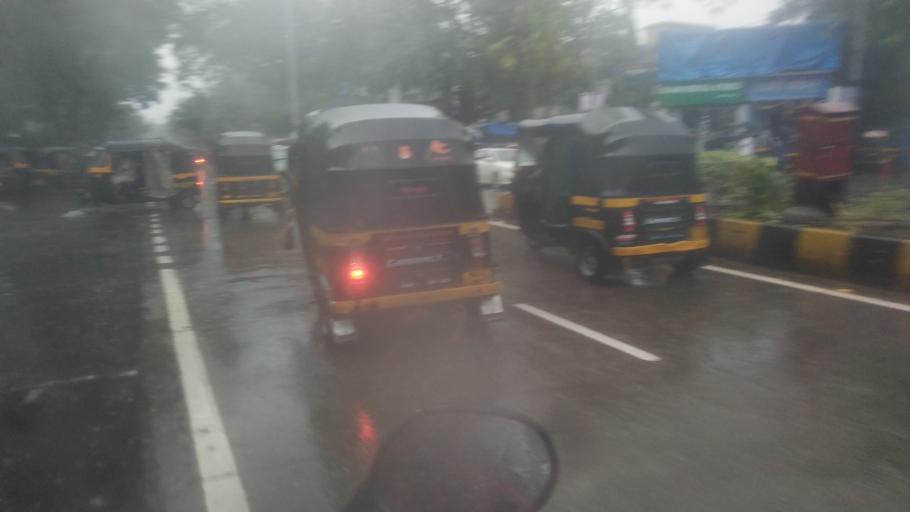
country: IN
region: Maharashtra
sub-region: Mumbai Suburban
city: Mumbai
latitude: 19.1034
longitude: 72.8335
